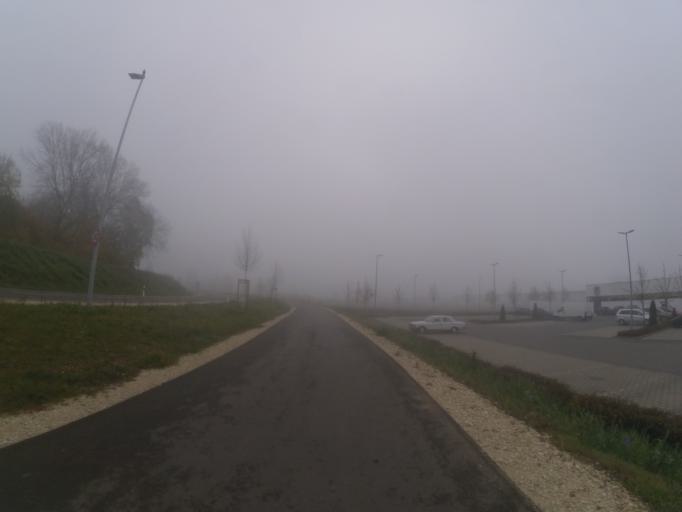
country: DE
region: Baden-Wuerttemberg
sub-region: Tuebingen Region
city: Ulm
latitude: 48.3516
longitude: 9.9804
